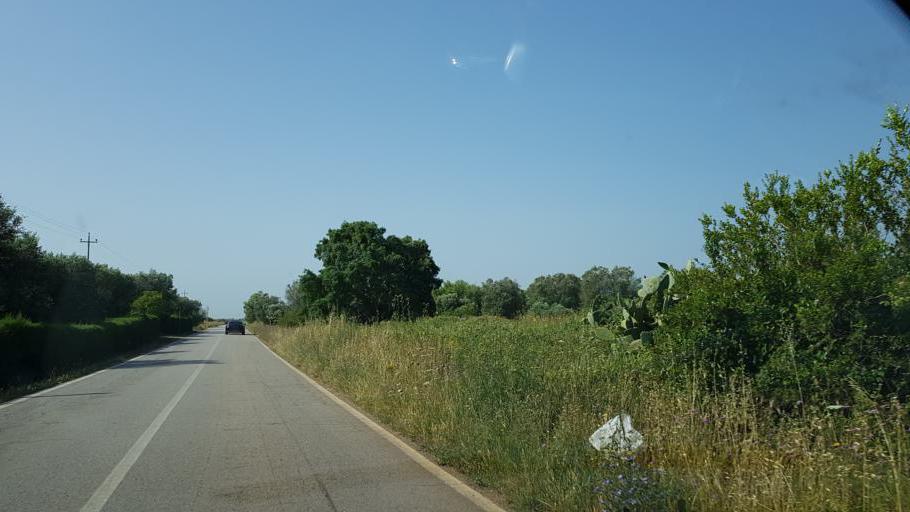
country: IT
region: Apulia
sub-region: Provincia di Brindisi
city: San Pancrazio Salentino
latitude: 40.4519
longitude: 17.8407
